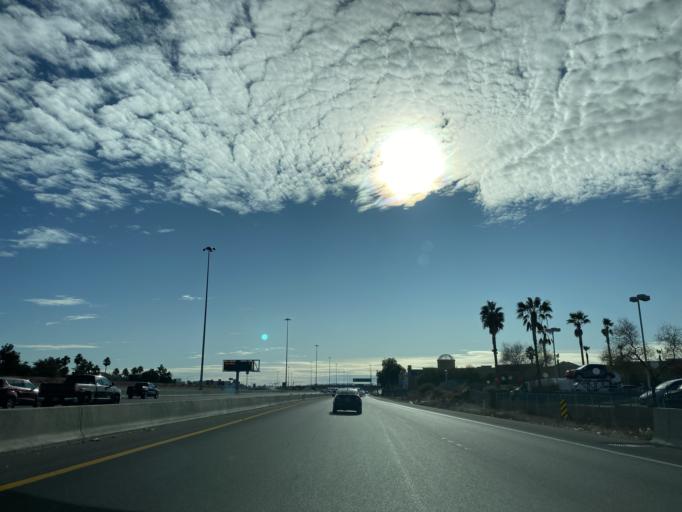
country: US
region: Nevada
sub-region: Clark County
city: Las Vegas
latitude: 36.2681
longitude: -115.2587
